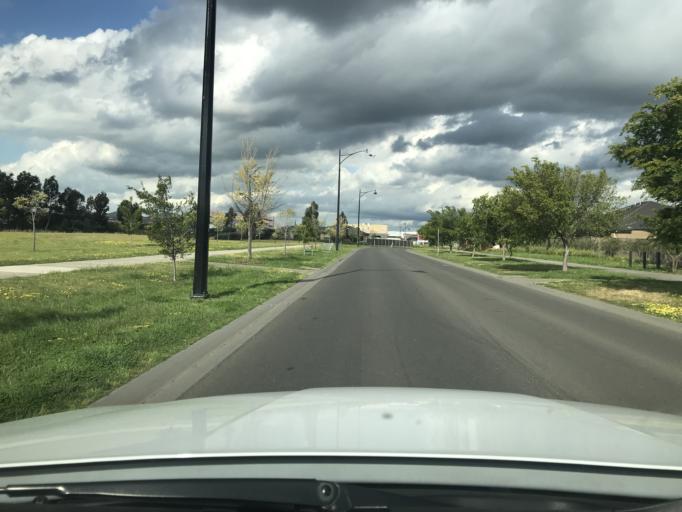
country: AU
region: Victoria
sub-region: Hume
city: Roxburgh Park
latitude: -37.5890
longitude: 144.9068
